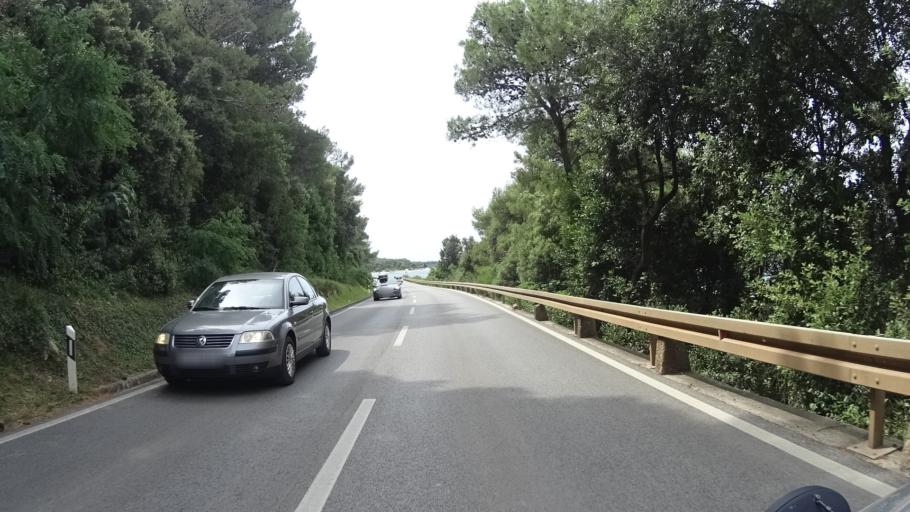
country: HR
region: Istarska
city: Medulin
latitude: 44.8150
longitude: 13.9098
